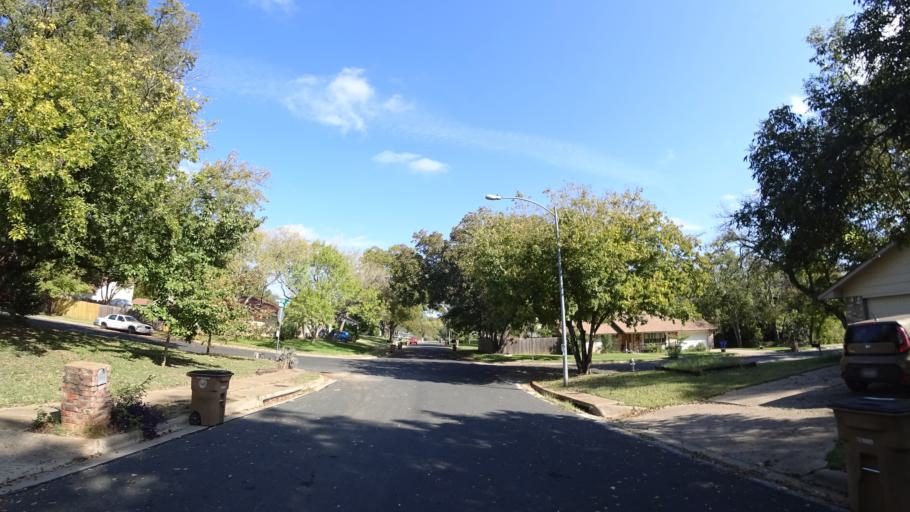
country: US
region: Texas
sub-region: Travis County
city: Shady Hollow
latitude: 30.1922
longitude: -97.8214
